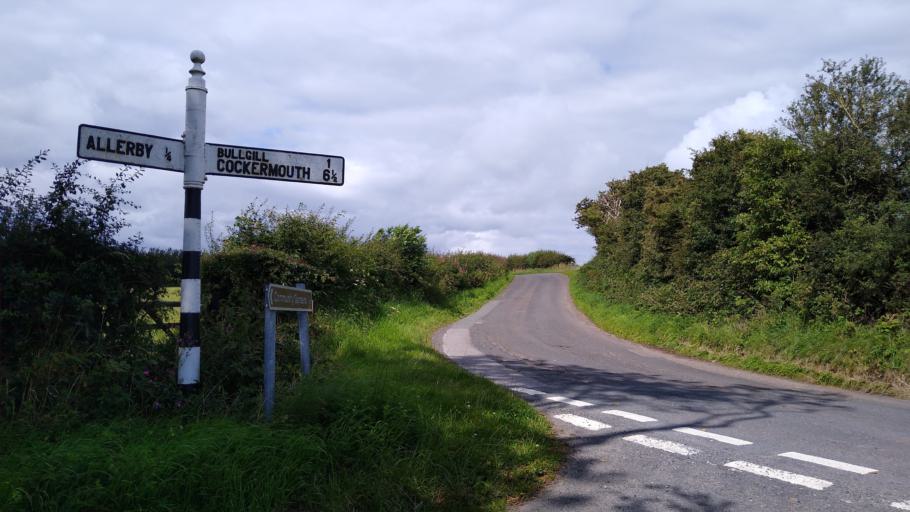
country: GB
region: England
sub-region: Cumbria
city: Dearham
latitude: 54.7441
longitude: -3.4114
